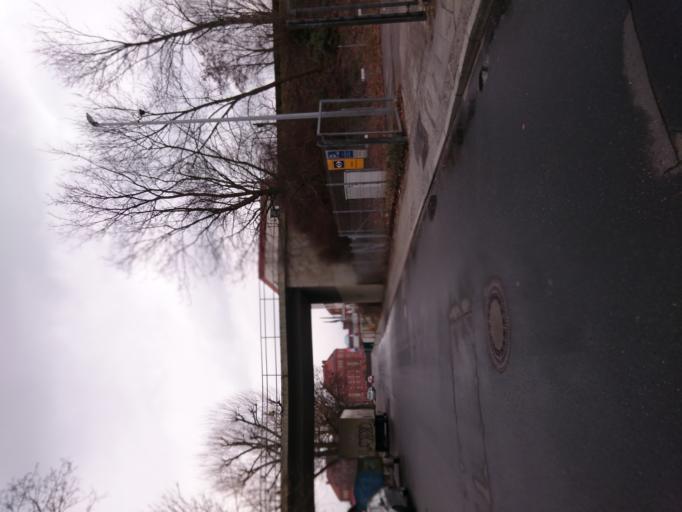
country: DE
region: Berlin
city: Tegel
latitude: 52.5741
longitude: 13.2989
